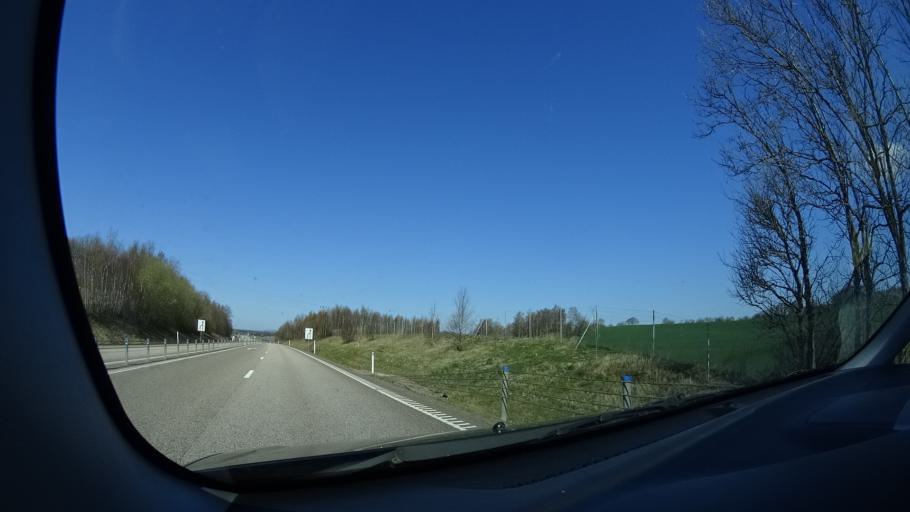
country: SE
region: Skane
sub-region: Astorps Kommun
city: Astorp
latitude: 56.1819
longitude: 12.8958
